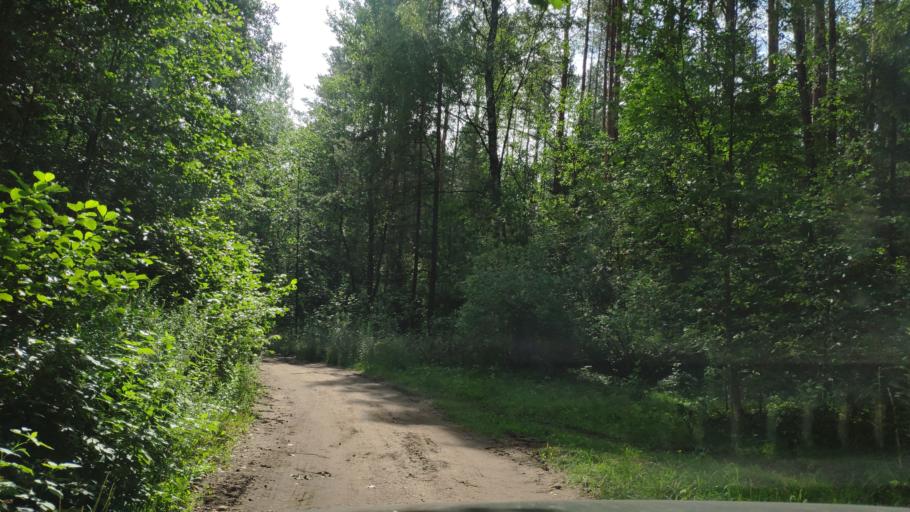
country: BY
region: Minsk
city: Zaslawye
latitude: 53.9740
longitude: 27.2894
